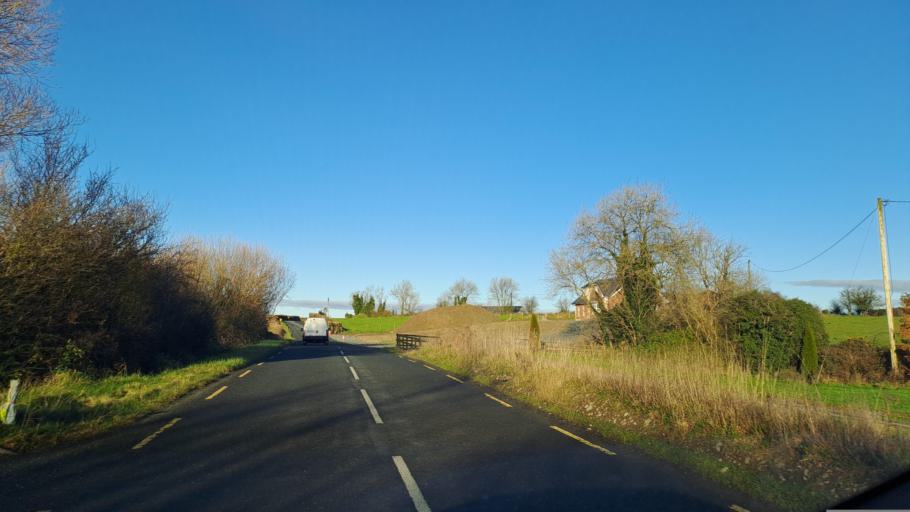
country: IE
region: Ulster
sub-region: An Cabhan
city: Mullagh
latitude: 53.8305
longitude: -6.9525
